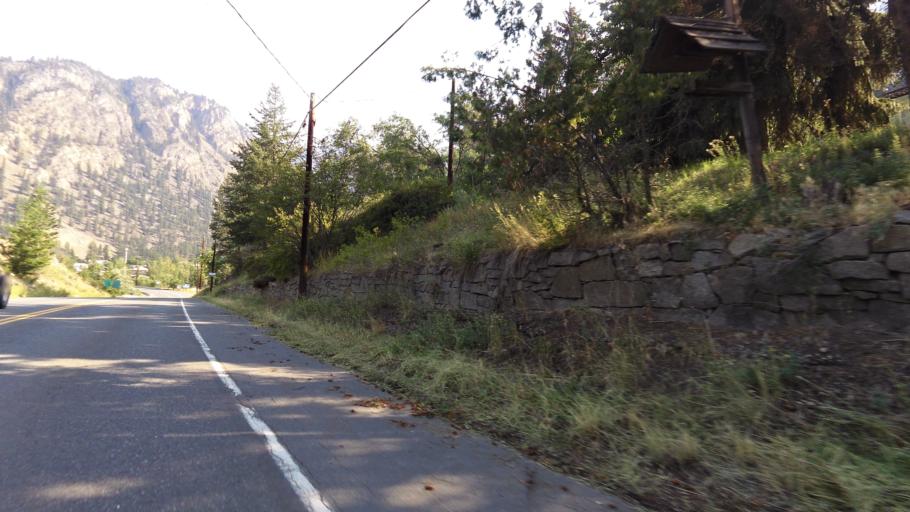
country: CA
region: British Columbia
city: Princeton
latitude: 49.3524
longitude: -120.0766
